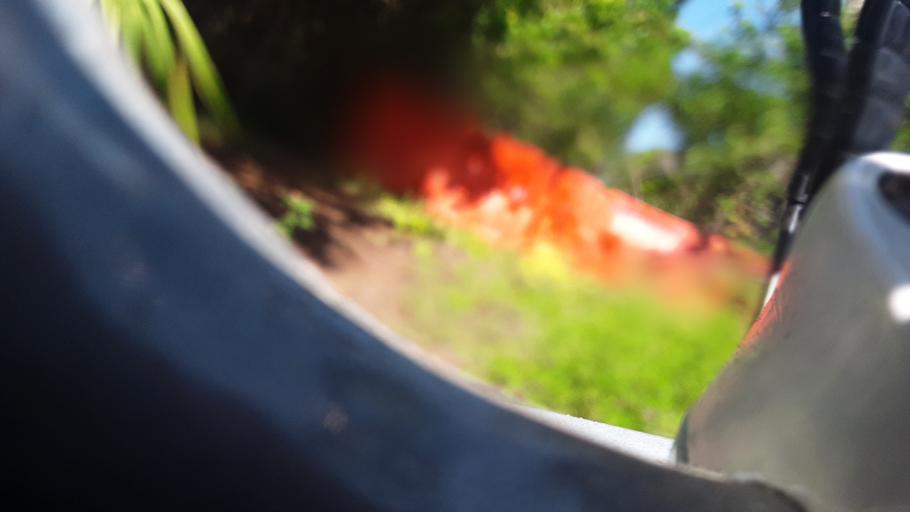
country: US
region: Florida
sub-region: Brevard County
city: Palm Bay
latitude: 27.9912
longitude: -80.6153
